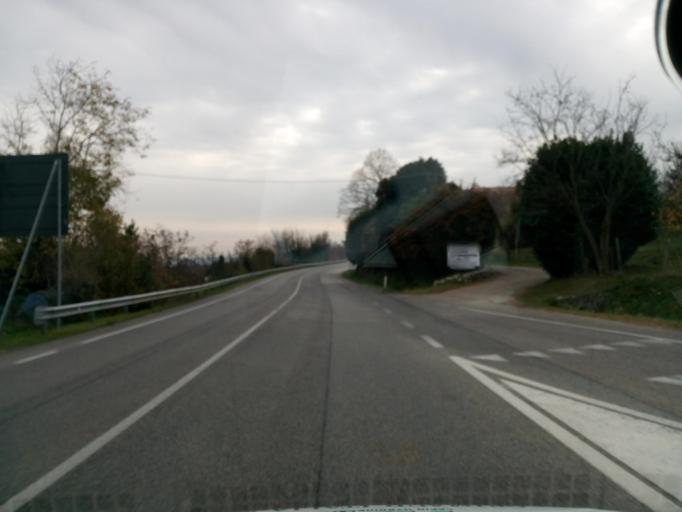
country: IT
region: Veneto
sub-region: Provincia di Treviso
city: Pederobba
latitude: 45.8725
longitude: 11.9660
